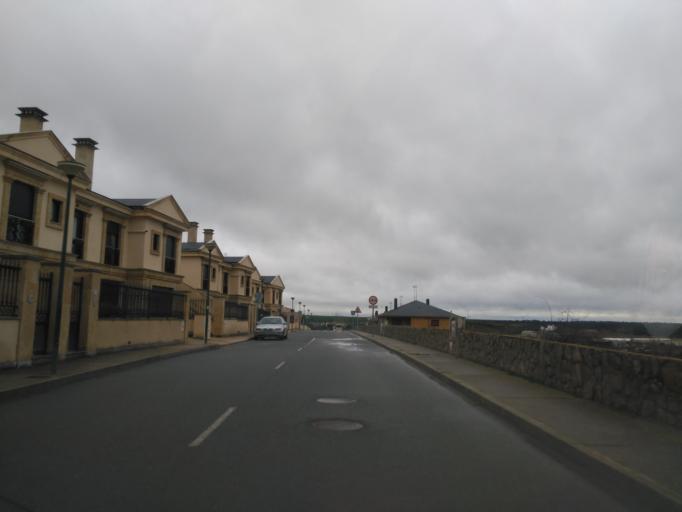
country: ES
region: Castille and Leon
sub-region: Provincia de Salamanca
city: Villamayor
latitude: 40.9804
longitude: -5.7042
